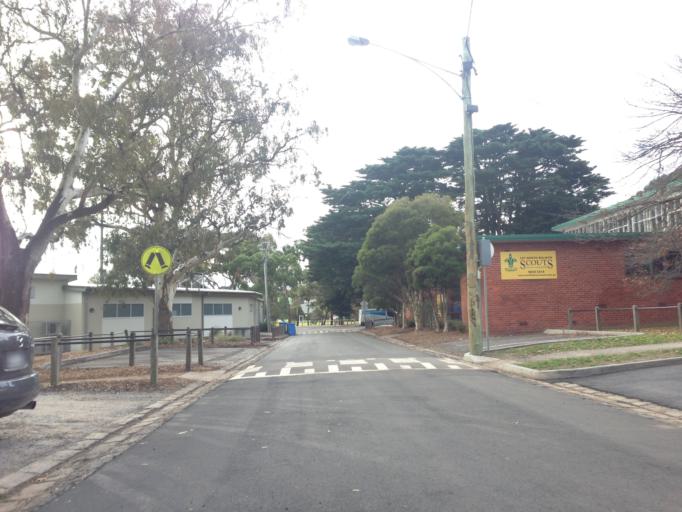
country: AU
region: Victoria
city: Balwyn
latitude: -37.8020
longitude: 145.0748
